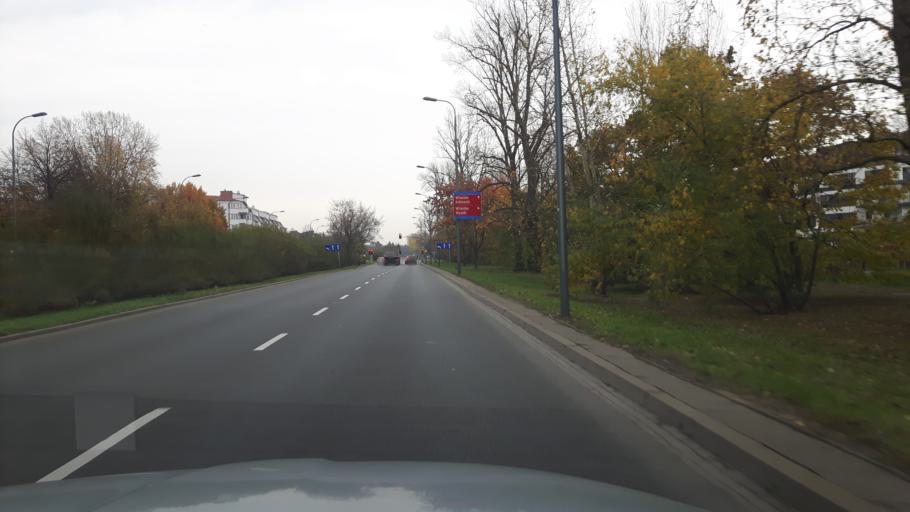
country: PL
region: Masovian Voivodeship
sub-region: Warszawa
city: Wilanow
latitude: 52.1686
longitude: 21.0729
